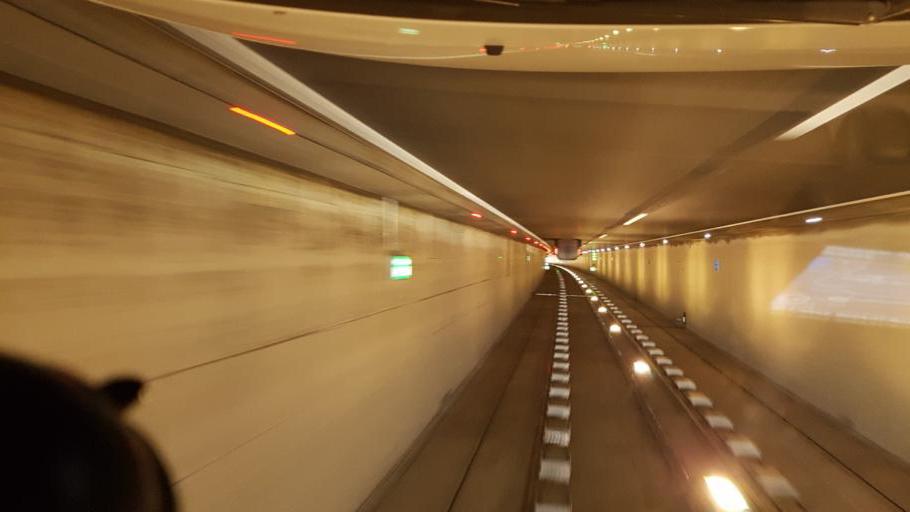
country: AT
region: Carinthia
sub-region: Politischer Bezirk Villach Land
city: Wernberg
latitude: 46.5951
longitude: 13.9472
